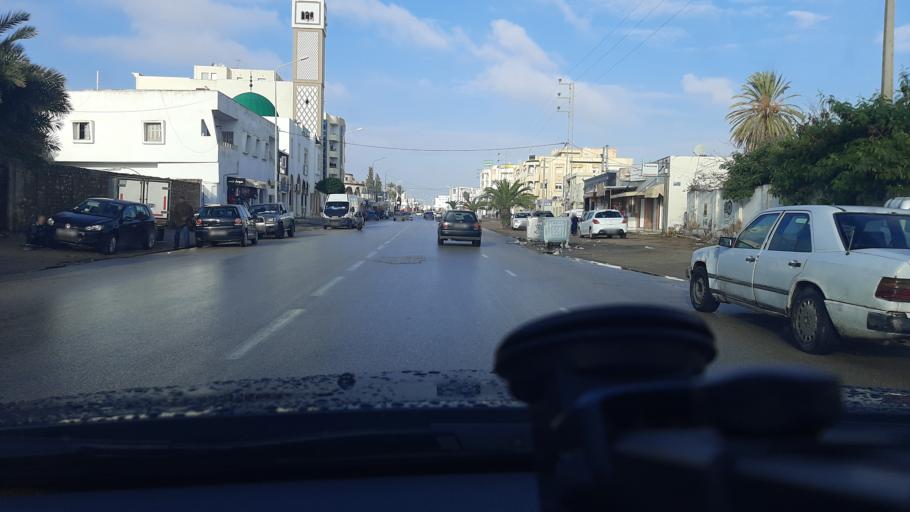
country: TN
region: Safaqis
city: Sfax
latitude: 34.7448
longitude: 10.7289
